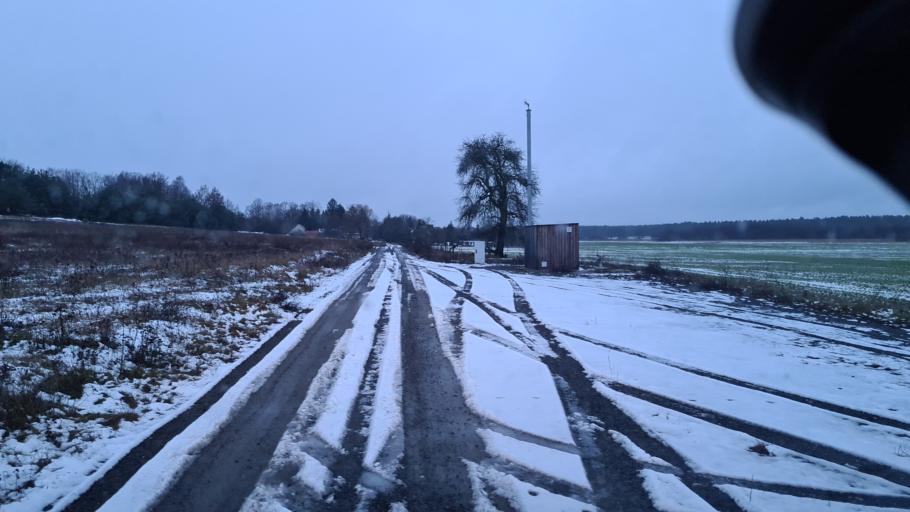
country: DE
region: Brandenburg
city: Schenkendobern
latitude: 51.9043
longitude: 14.5847
